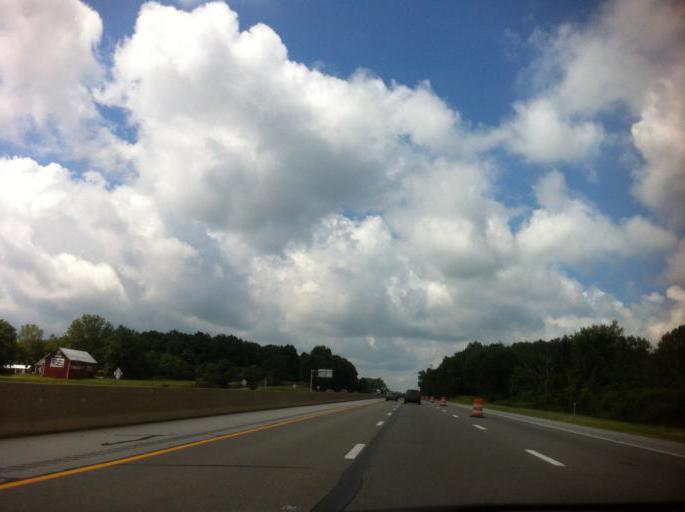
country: US
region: Ohio
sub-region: Huron County
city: Wakeman
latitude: 41.3298
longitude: -82.4674
